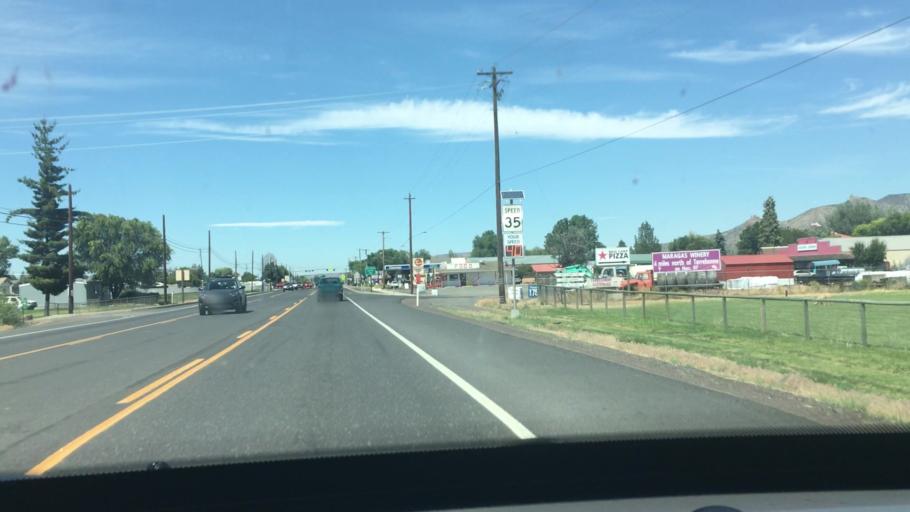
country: US
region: Oregon
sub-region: Deschutes County
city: Terrebonne
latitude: 44.3484
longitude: -121.1787
